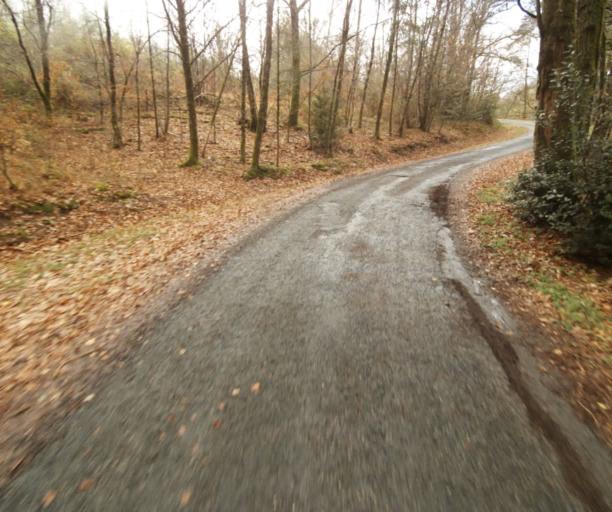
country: FR
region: Limousin
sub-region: Departement de la Correze
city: Saint-Privat
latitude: 45.2190
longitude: 2.0266
